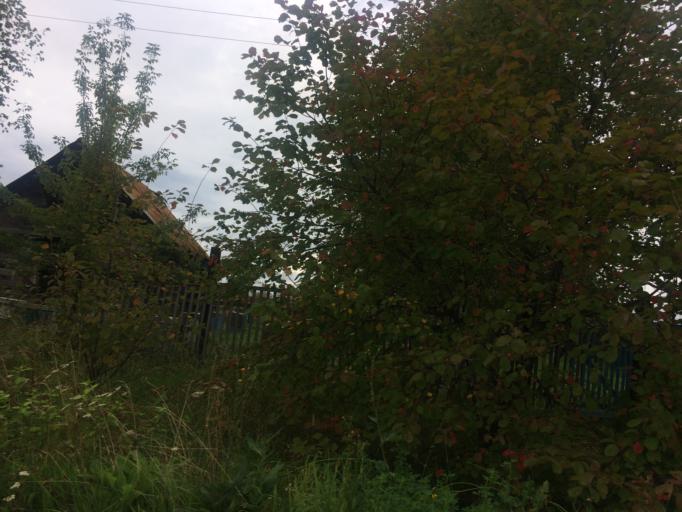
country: RU
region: Primorskiy
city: Lazo
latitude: 45.8300
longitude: 133.6185
